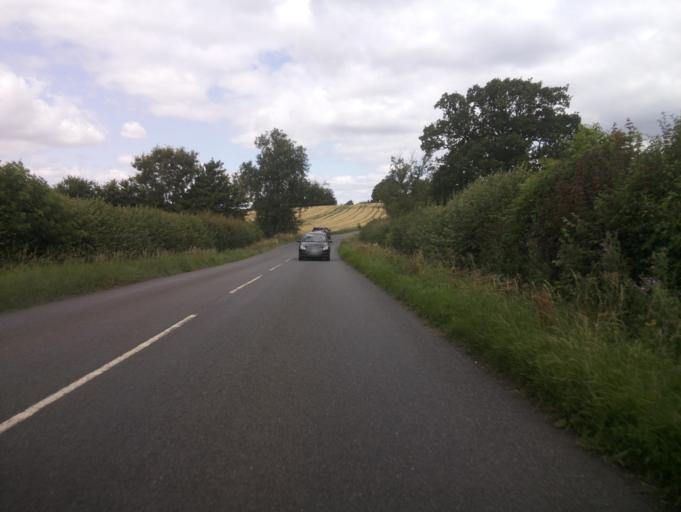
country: GB
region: England
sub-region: Buckinghamshire
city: Newton Longville
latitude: 51.9730
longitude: -0.8200
